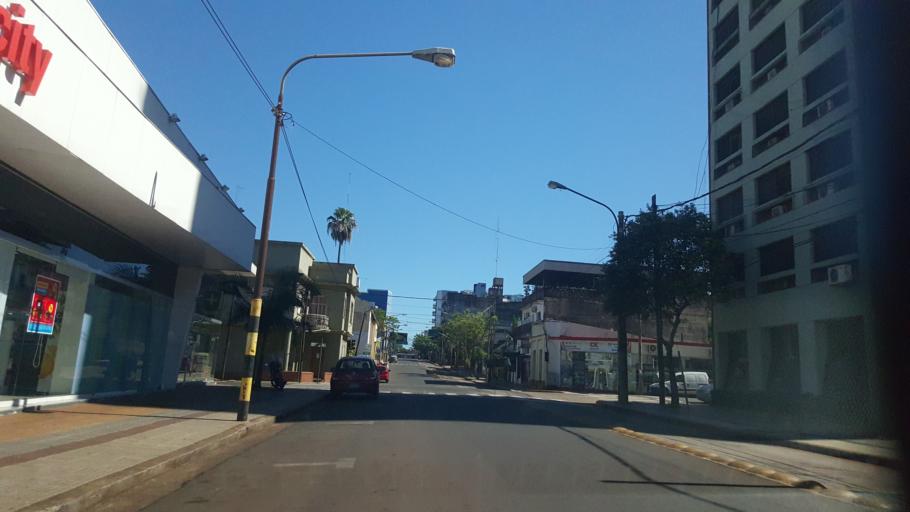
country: AR
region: Misiones
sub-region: Departamento de Capital
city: Posadas
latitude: -27.3708
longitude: -55.8983
